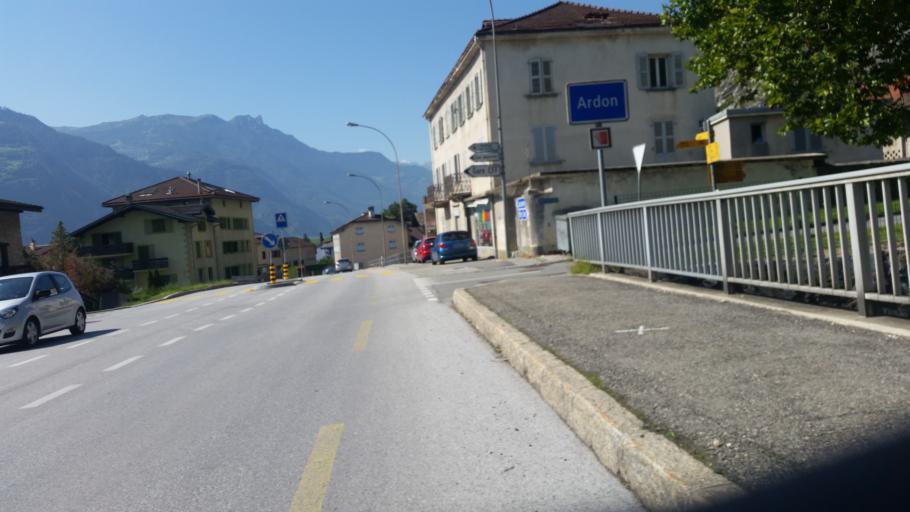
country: CH
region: Valais
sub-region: Conthey District
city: Ardon
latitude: 46.2156
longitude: 7.2589
